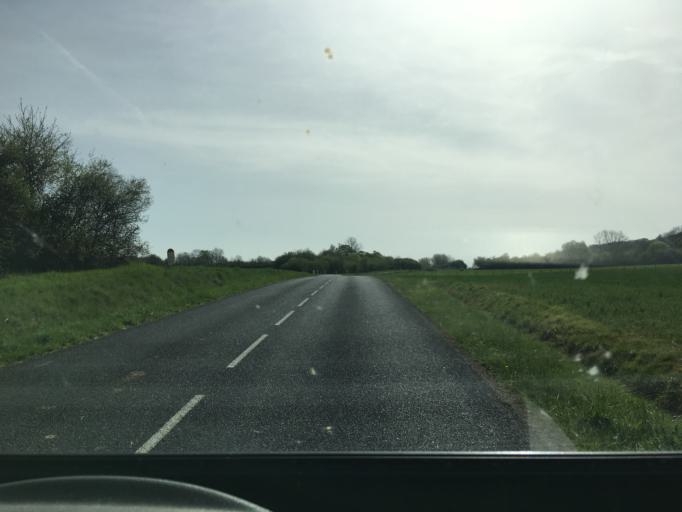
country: FR
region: Lorraine
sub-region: Departement de Meurthe-et-Moselle
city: Dommartin-les-Toul
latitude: 48.6709
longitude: 5.9336
